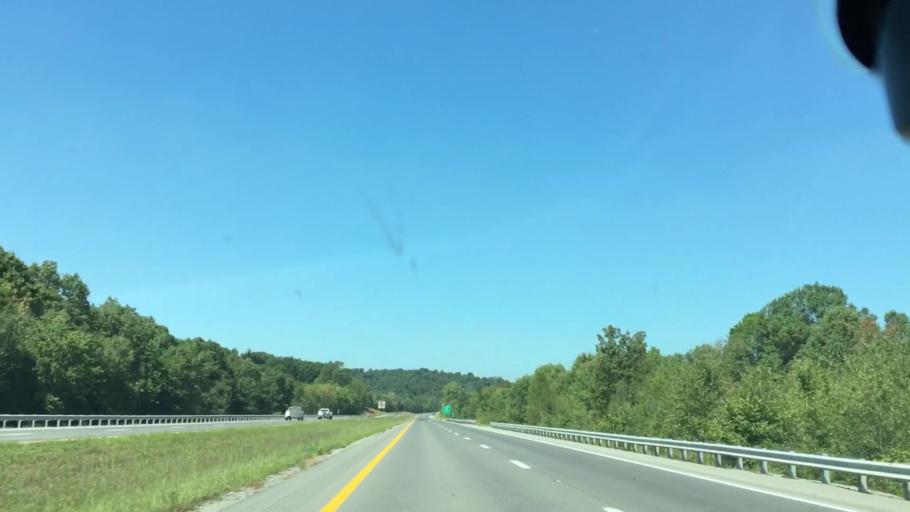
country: US
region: Kentucky
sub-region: Webster County
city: Sebree
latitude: 37.5875
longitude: -87.4894
